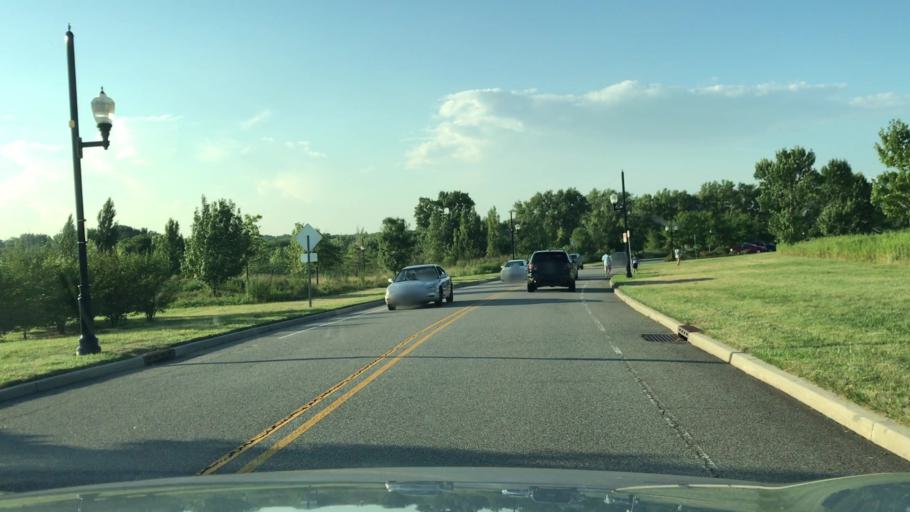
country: US
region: New Jersey
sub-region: Bergen County
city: Ridgefield Park
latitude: 40.8632
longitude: -74.0063
